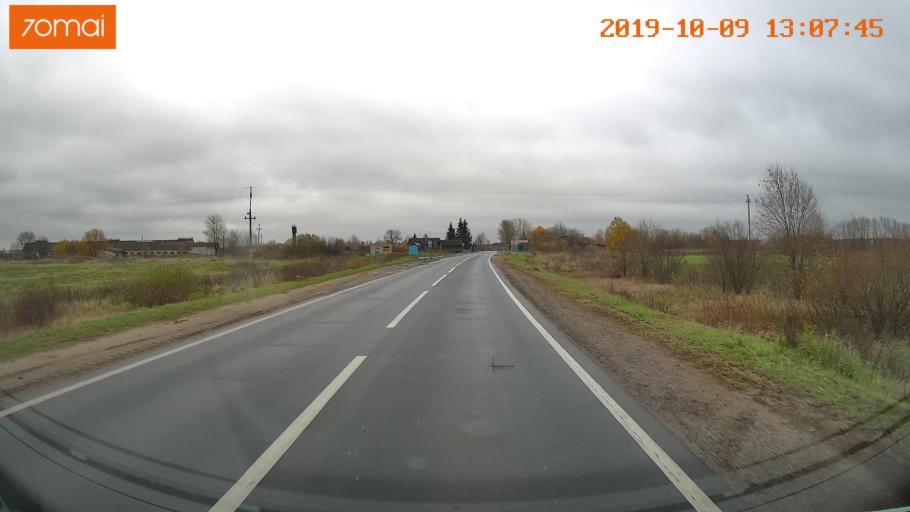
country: RU
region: Jaroslavl
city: Lyubim
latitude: 58.3568
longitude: 40.6507
